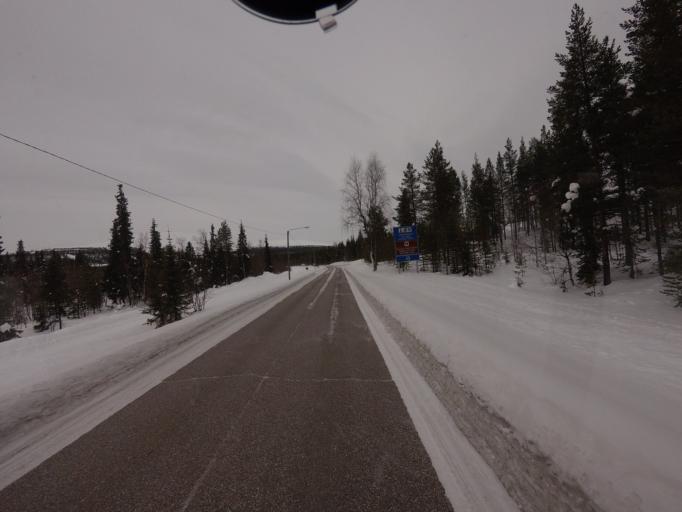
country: FI
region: Lapland
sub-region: Tunturi-Lappi
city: Kolari
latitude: 67.5349
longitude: 24.2771
